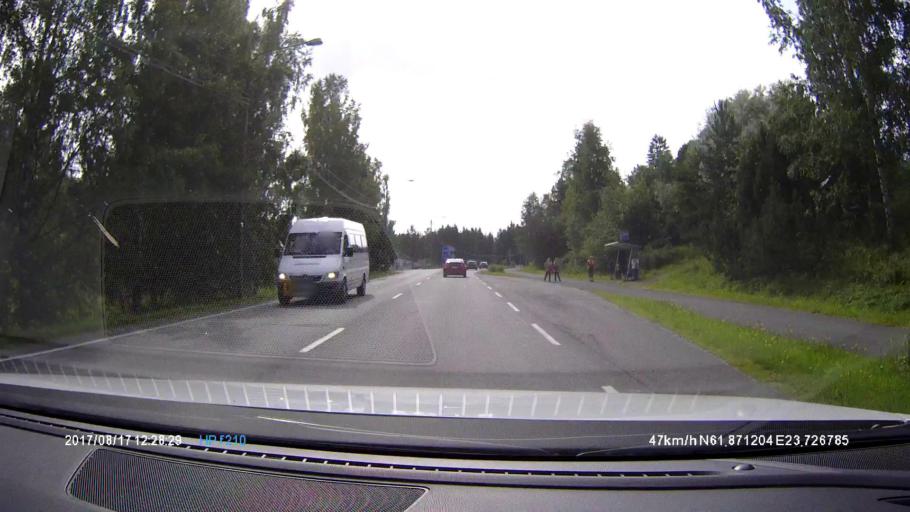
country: FI
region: Pirkanmaa
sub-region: Tampere
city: Kuru
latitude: 61.8710
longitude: 23.7268
